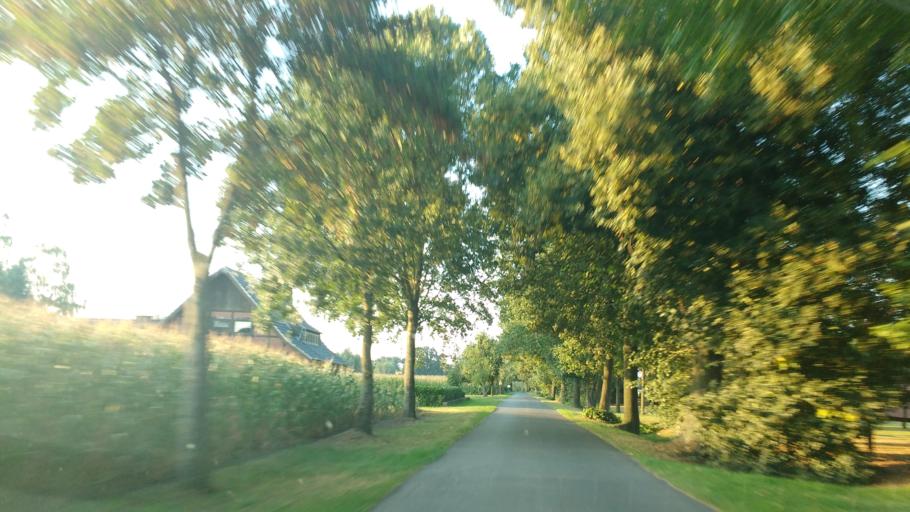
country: DE
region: North Rhine-Westphalia
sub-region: Regierungsbezirk Detmold
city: Delbruck
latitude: 51.7494
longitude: 8.5262
